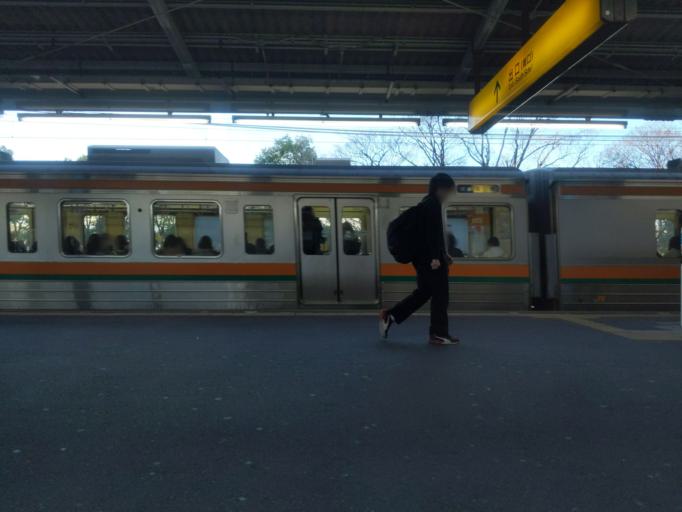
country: JP
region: Aichi
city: Nagoya-shi
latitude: 35.1890
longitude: 136.9371
